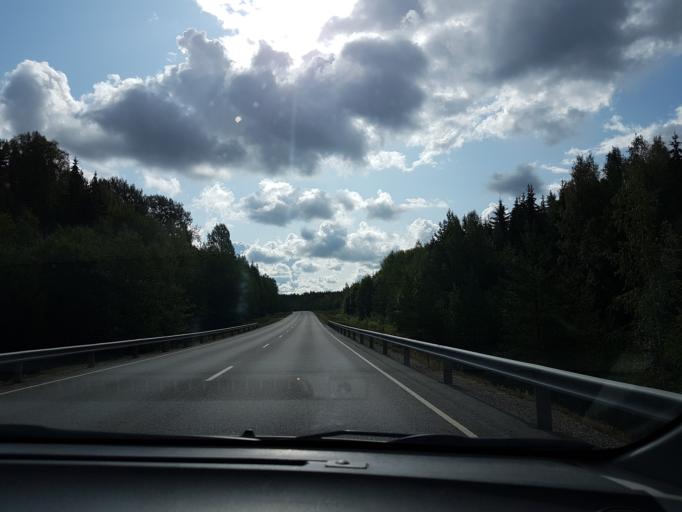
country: FI
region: Uusimaa
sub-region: Helsinki
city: Sibbo
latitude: 60.4727
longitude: 25.2361
